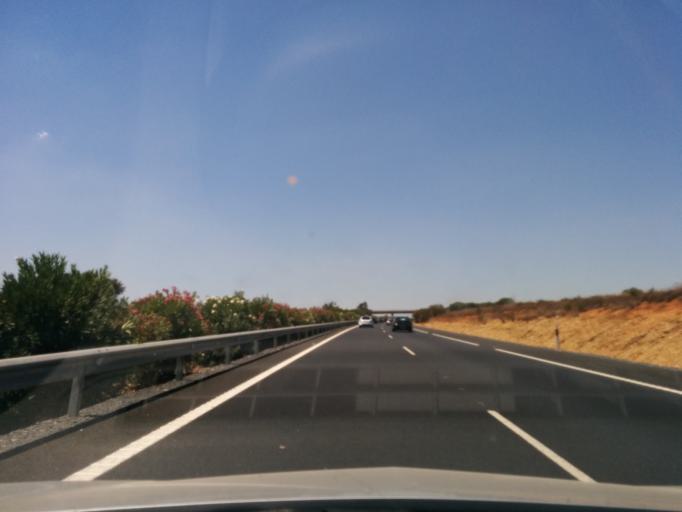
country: ES
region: Andalusia
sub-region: Provincia de Huelva
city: Lucena del Puerto
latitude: 37.3358
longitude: -6.7617
